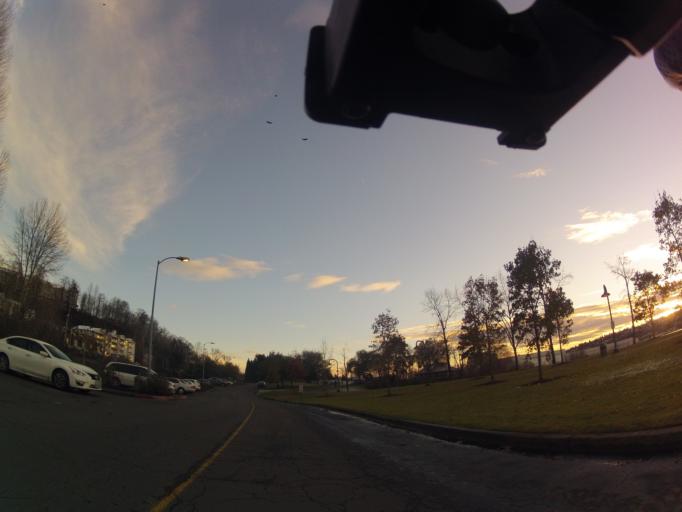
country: US
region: Washington
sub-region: King County
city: Renton
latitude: 47.5100
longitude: -122.2029
